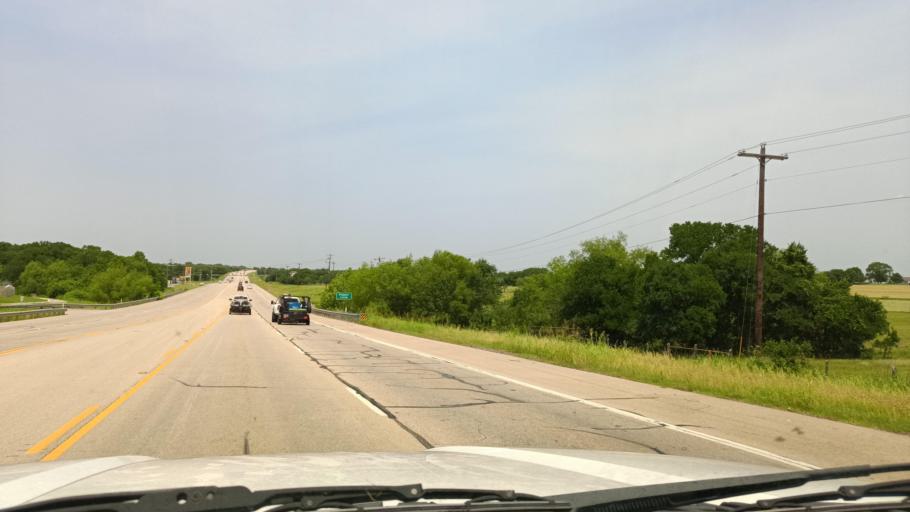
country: US
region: Texas
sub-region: Bell County
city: Temple
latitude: 31.1261
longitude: -97.3950
